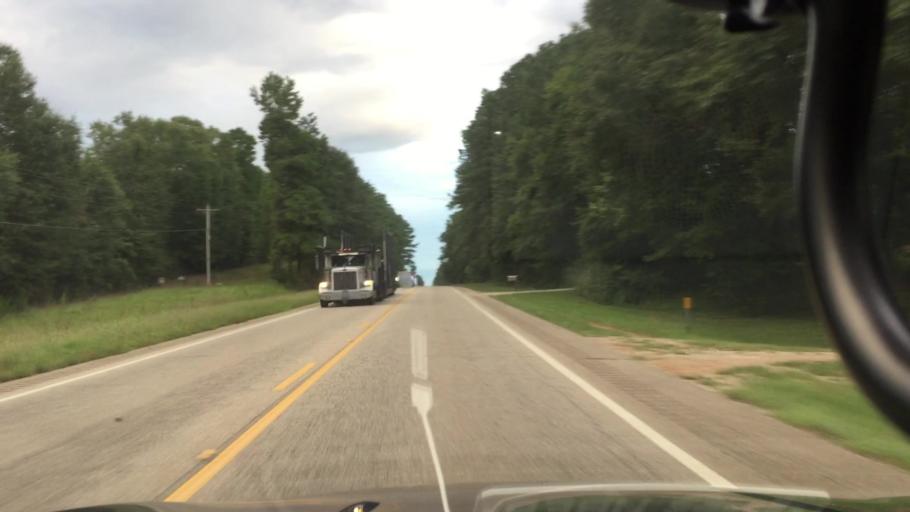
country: US
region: Alabama
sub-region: Pike County
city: Troy
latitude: 31.6616
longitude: -85.9529
